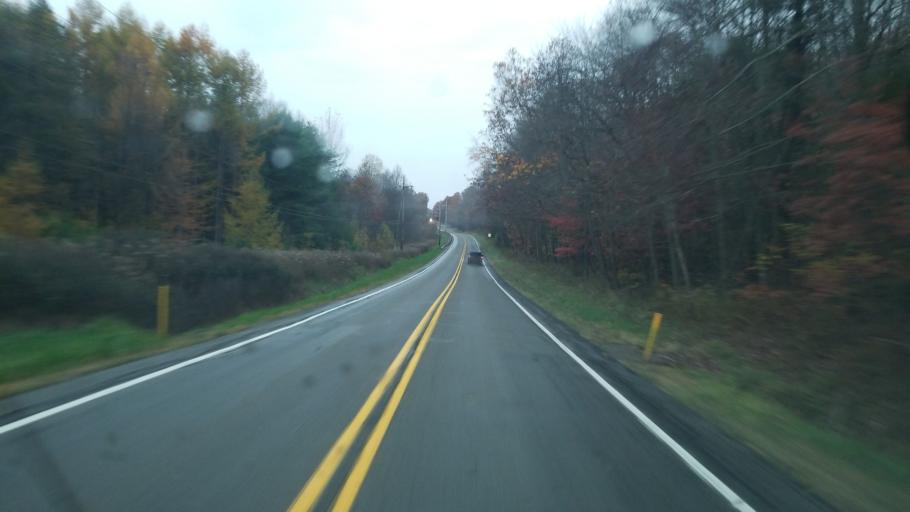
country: US
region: Pennsylvania
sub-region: Clarion County
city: Marianne
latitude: 41.2849
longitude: -79.3857
